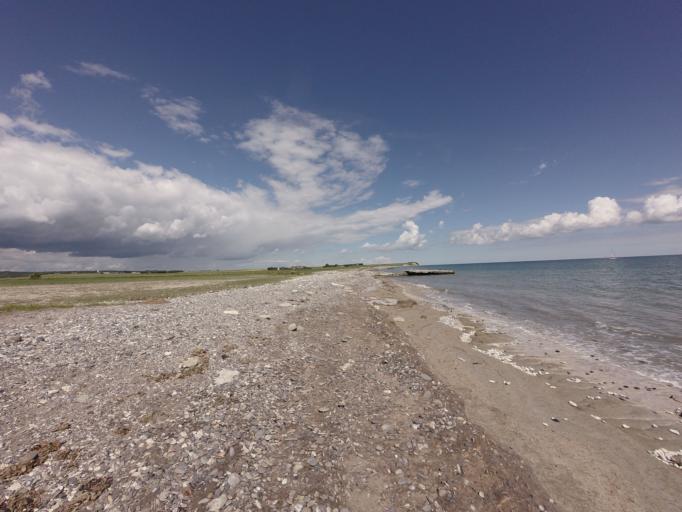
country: DK
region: Central Jutland
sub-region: Norddjurs Kommune
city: Grenaa
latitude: 56.4895
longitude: 10.8739
